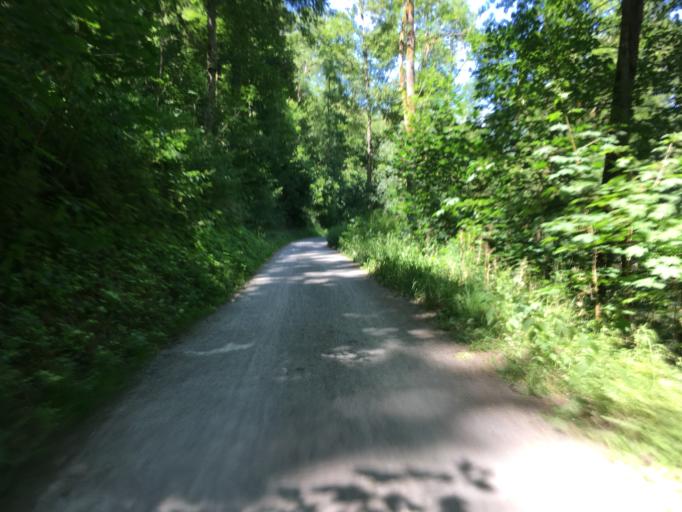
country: DE
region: Baden-Wuerttemberg
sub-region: Regierungsbezirk Stuttgart
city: Vaihingen an der Enz
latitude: 48.9185
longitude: 8.9521
